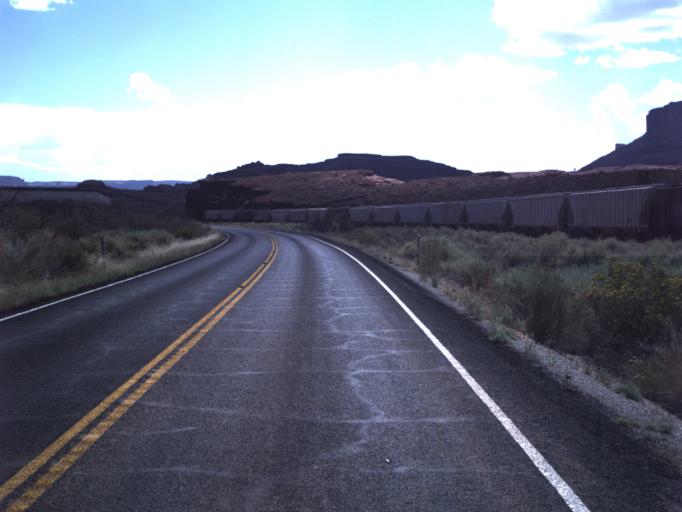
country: US
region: Utah
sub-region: Grand County
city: Moab
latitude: 38.5338
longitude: -109.6563
